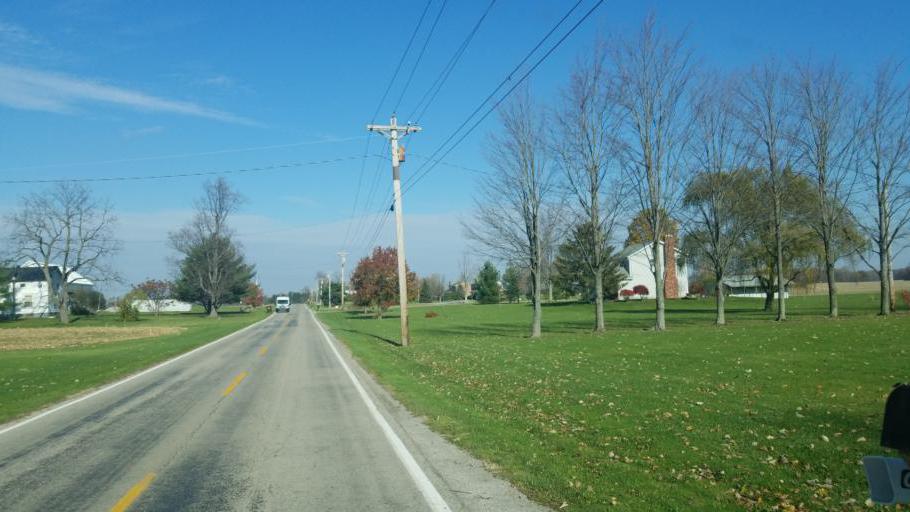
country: US
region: Ohio
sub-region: Lorain County
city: Wellington
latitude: 41.1934
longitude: -82.2685
